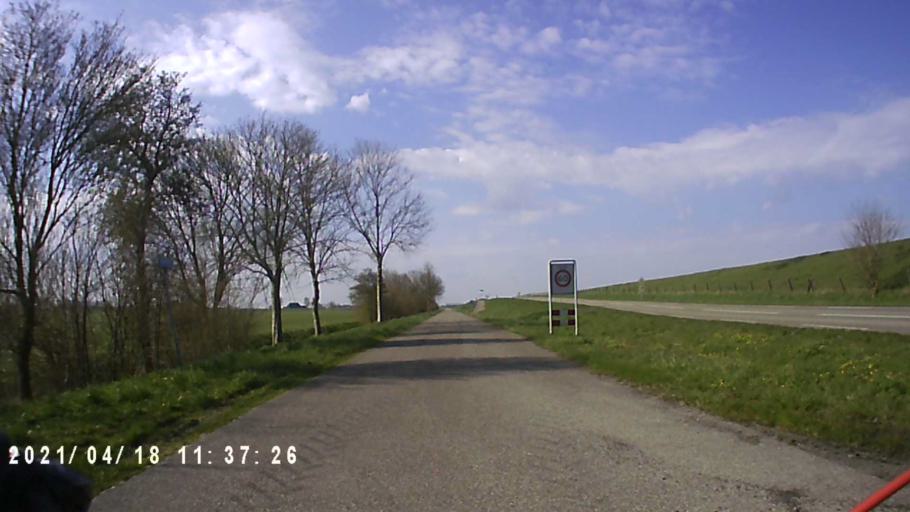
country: NL
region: Groningen
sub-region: Gemeente Zuidhorn
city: Grijpskerk
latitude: 53.3165
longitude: 6.2674
